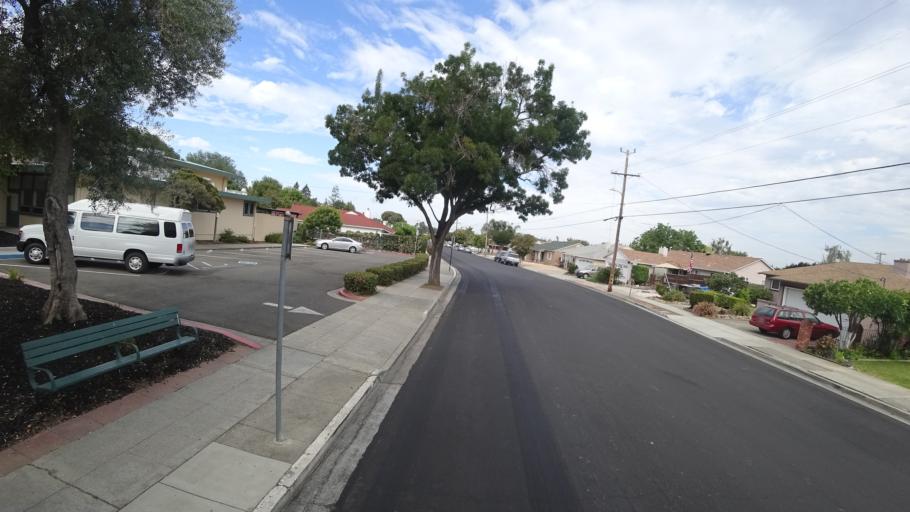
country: US
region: California
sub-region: Alameda County
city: Hayward
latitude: 37.6447
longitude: -122.0713
